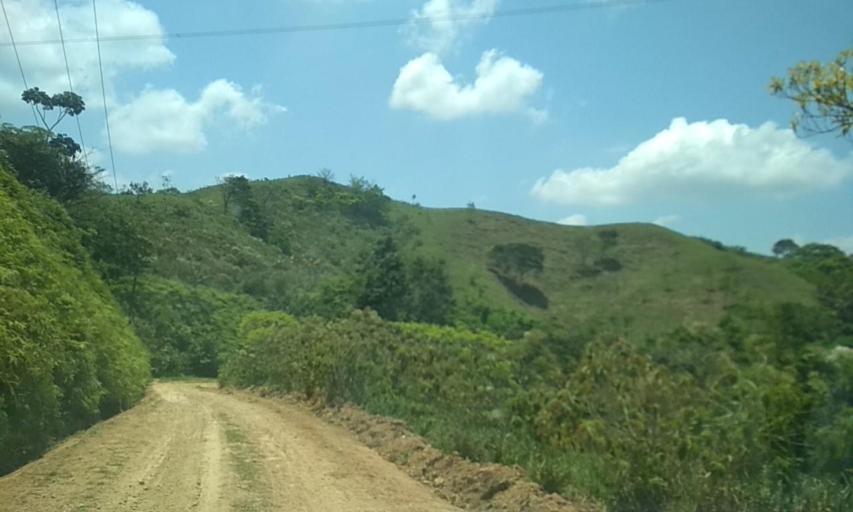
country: MX
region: Chiapas
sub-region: Tecpatan
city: Raudales Malpaso
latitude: 17.3978
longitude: -93.7466
